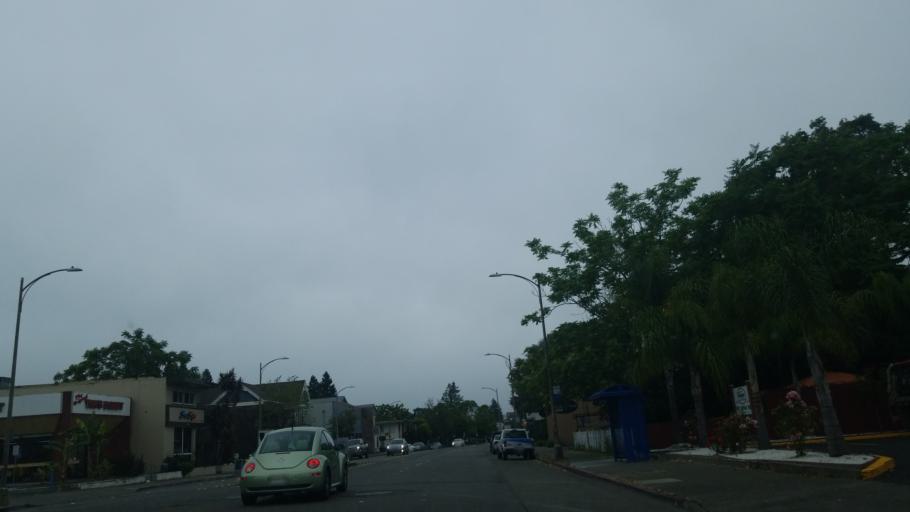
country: US
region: California
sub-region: Sonoma County
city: Santa Rosa
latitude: 38.4449
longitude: -122.7050
